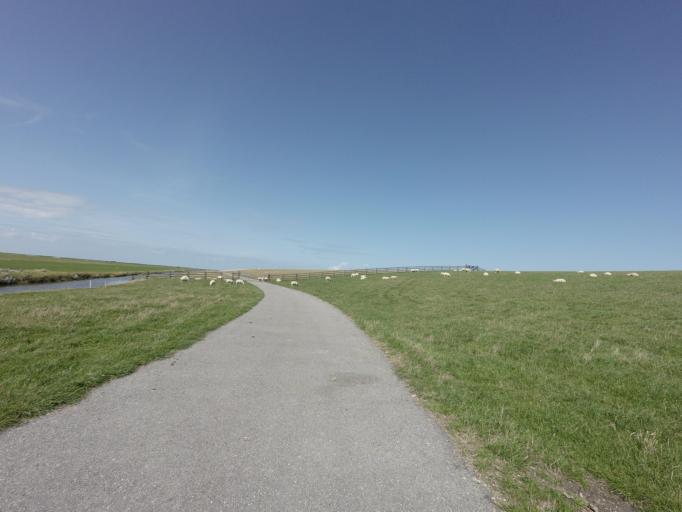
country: NL
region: Friesland
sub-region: Gemeente Dongeradeel
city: Holwerd
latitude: 53.3666
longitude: 5.8618
